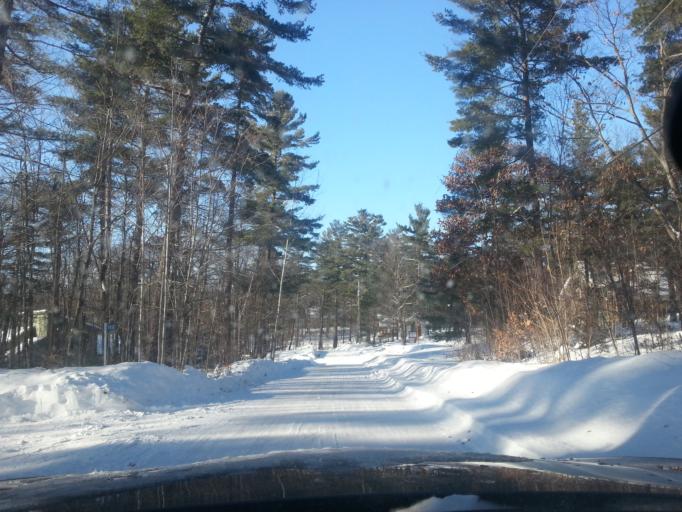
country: CA
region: Ontario
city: Arnprior
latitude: 45.3247
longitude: -76.3260
